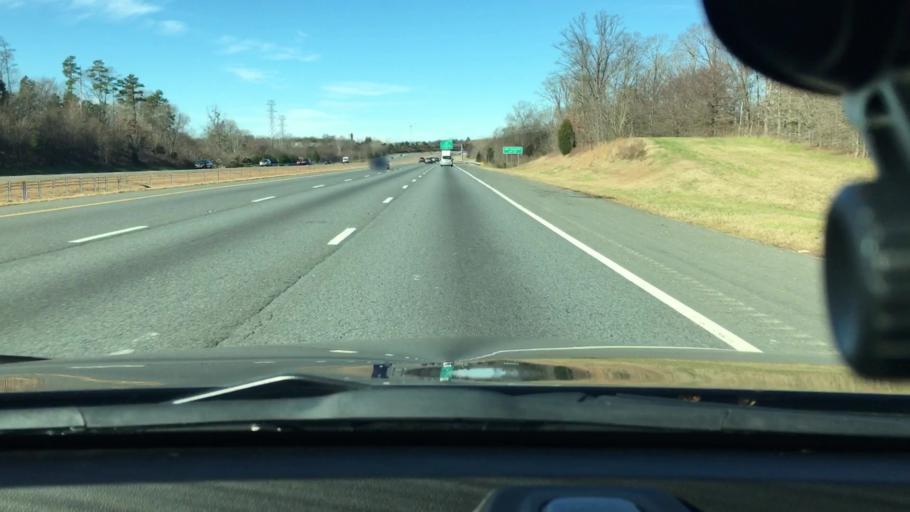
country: US
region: North Carolina
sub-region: Cabarrus County
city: Harrisburg
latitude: 35.3070
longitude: -80.6952
